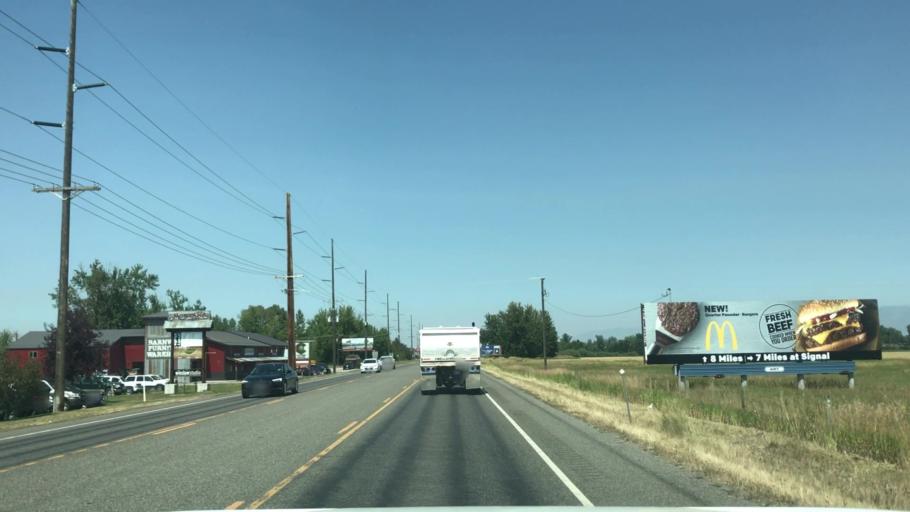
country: US
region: Montana
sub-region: Gallatin County
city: Four Corners
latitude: 45.6619
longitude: -111.1857
